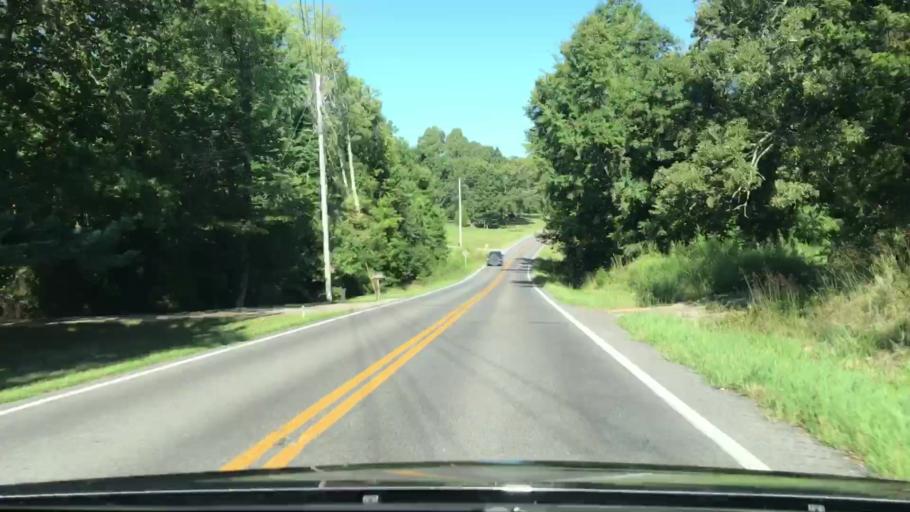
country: US
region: Kentucky
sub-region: Graves County
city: Mayfield
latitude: 36.7736
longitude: -88.5017
